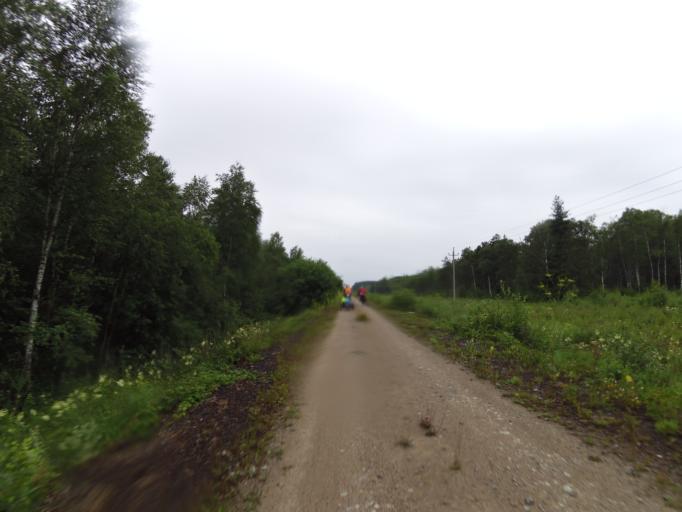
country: EE
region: Harju
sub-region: Nissi vald
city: Turba
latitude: 58.9860
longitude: 23.9313
